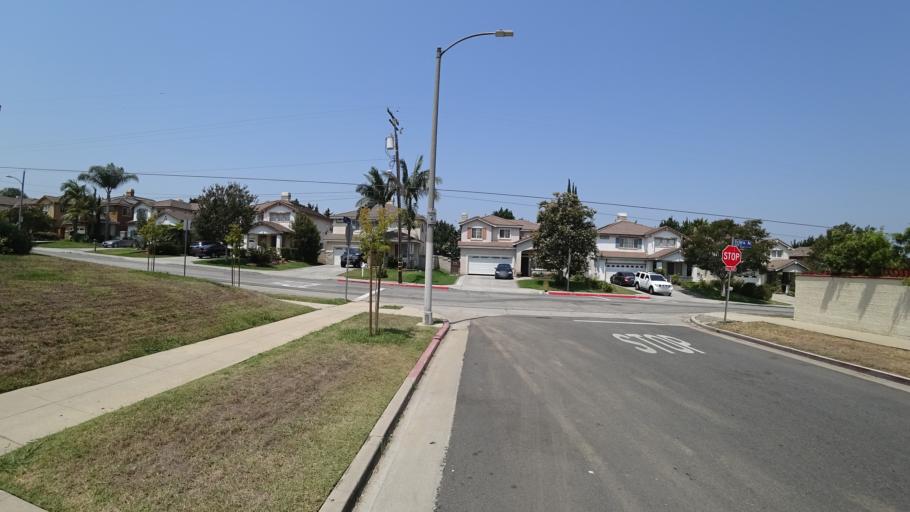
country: US
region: California
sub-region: Los Angeles County
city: Inglewood
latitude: 33.9700
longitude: -118.3328
